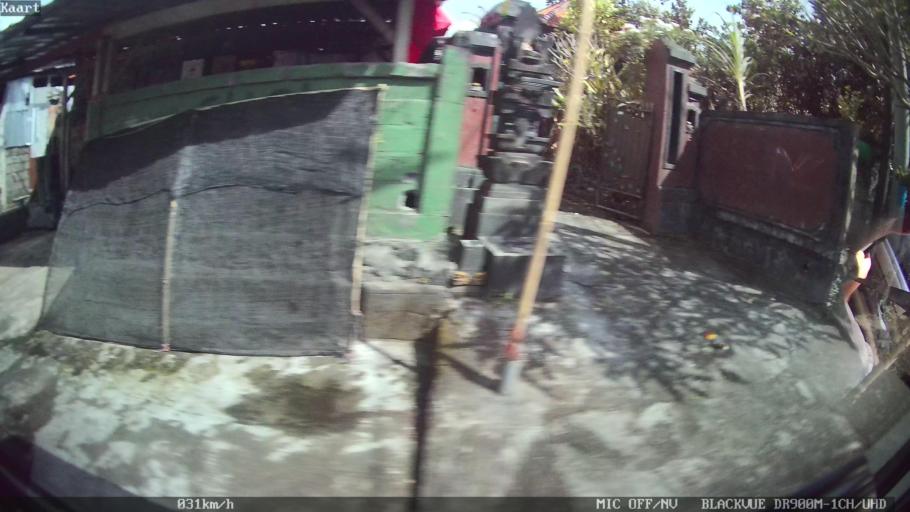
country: ID
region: Bali
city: Banjar Karangsuling
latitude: -8.6076
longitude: 115.2038
